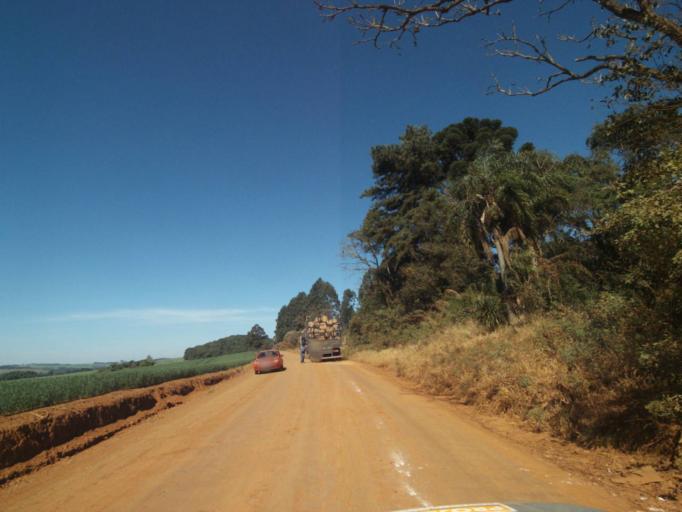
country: BR
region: Parana
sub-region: Tibagi
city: Tibagi
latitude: -24.5851
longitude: -50.6100
